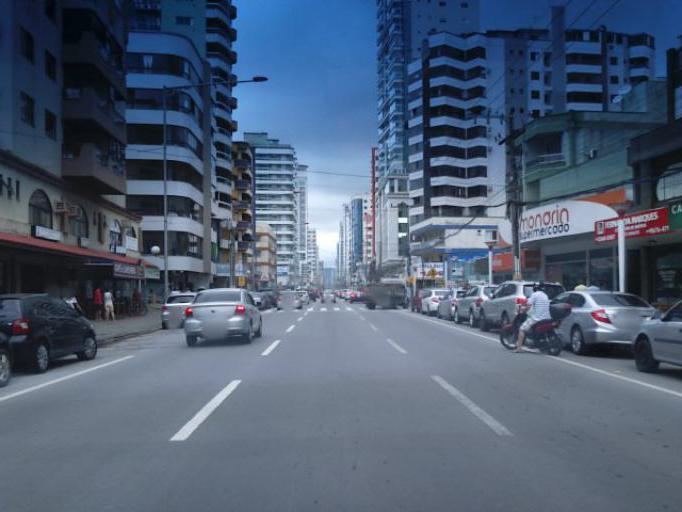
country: BR
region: Santa Catarina
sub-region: Itapema
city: Itapema
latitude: -27.1197
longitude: -48.6076
